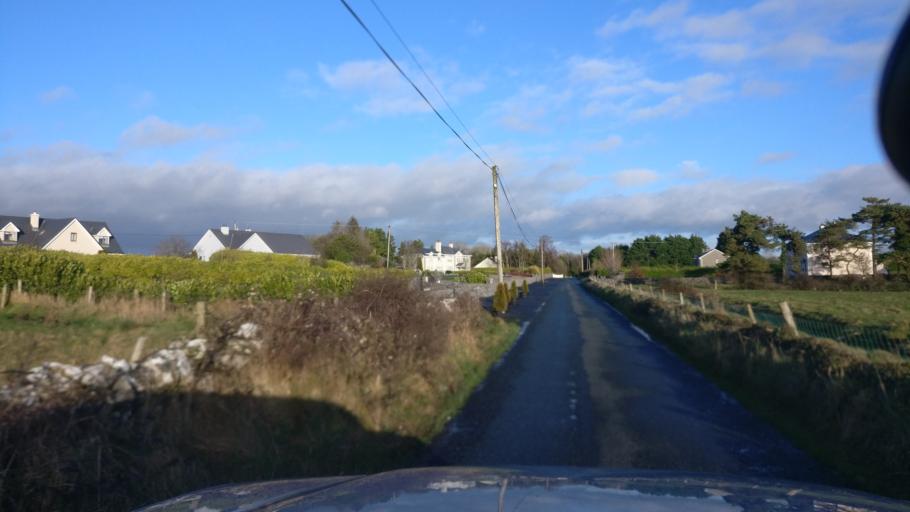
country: IE
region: Connaught
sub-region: County Galway
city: Loughrea
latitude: 53.2245
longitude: -8.5564
